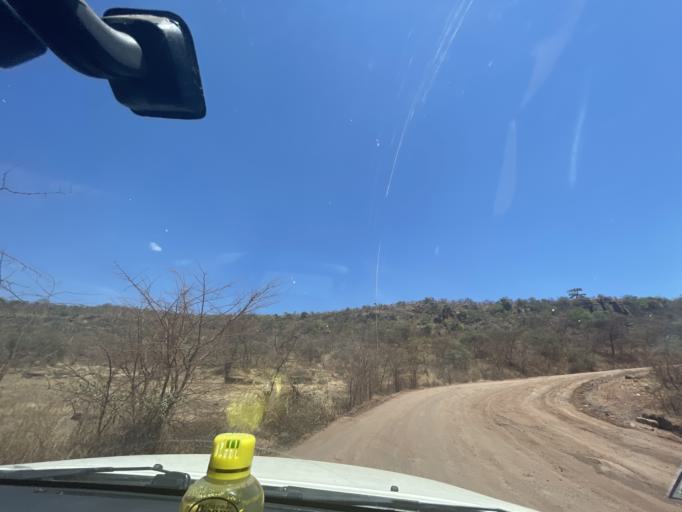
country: ET
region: Amhara
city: Bure
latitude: 10.3878
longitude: 37.0271
